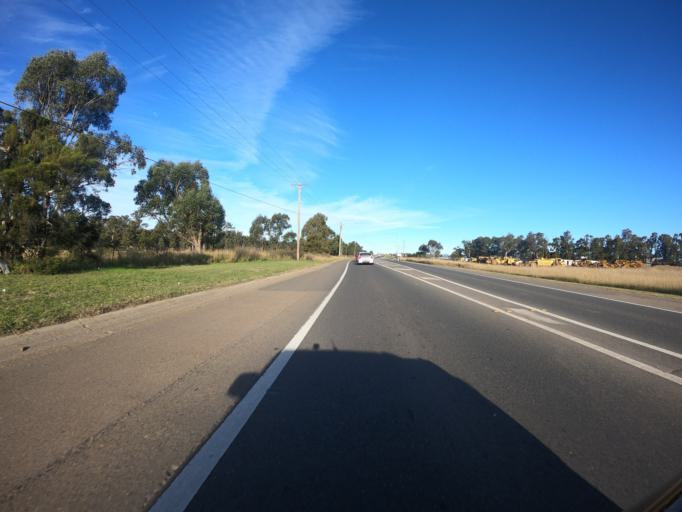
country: AU
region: New South Wales
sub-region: Blacktown
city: Riverstone
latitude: -33.6871
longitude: 150.8228
